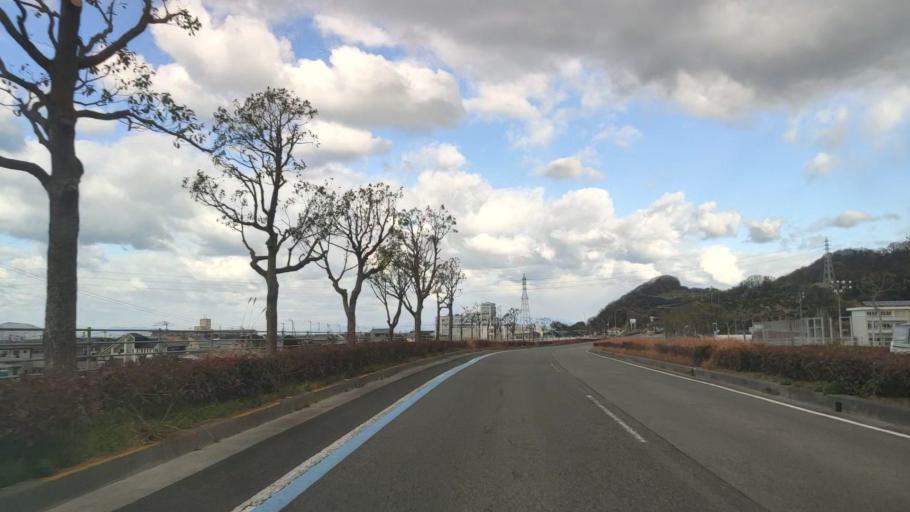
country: JP
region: Ehime
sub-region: Shikoku-chuo Shi
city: Matsuyama
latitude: 33.9001
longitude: 132.7571
